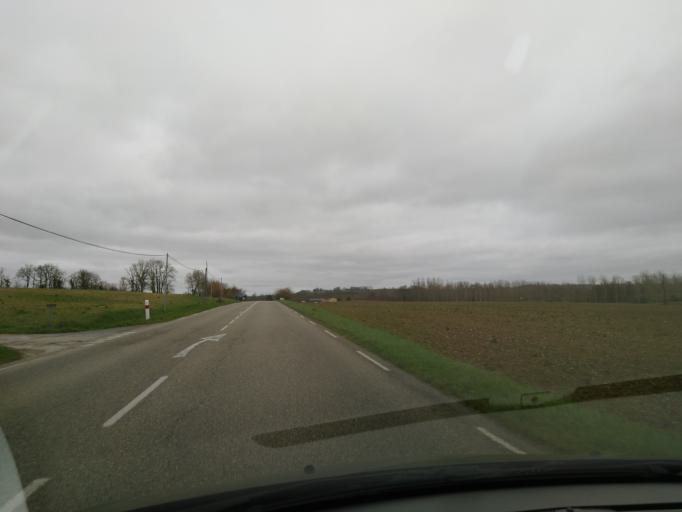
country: FR
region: Aquitaine
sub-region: Departement du Lot-et-Garonne
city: Castillonnes
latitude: 44.6633
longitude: 0.5848
